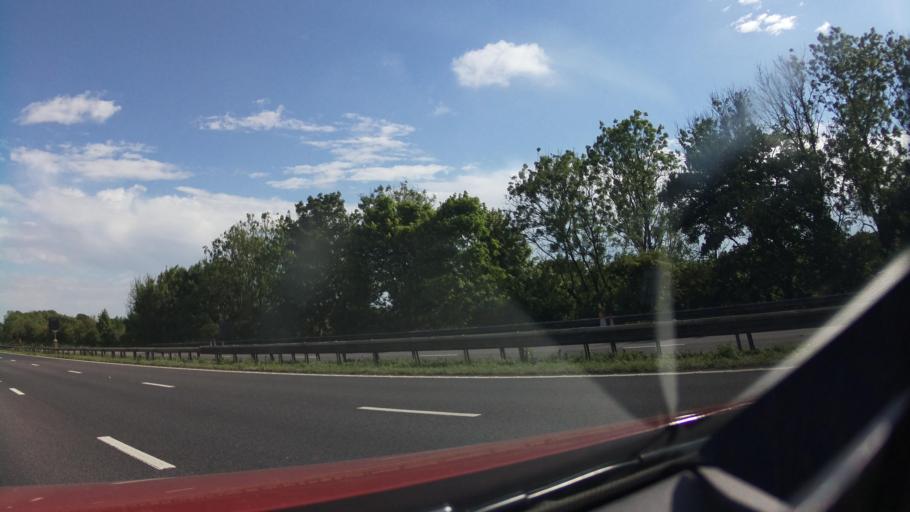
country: GB
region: England
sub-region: Borough of Wigan
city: Haigh
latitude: 53.6085
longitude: -2.5800
